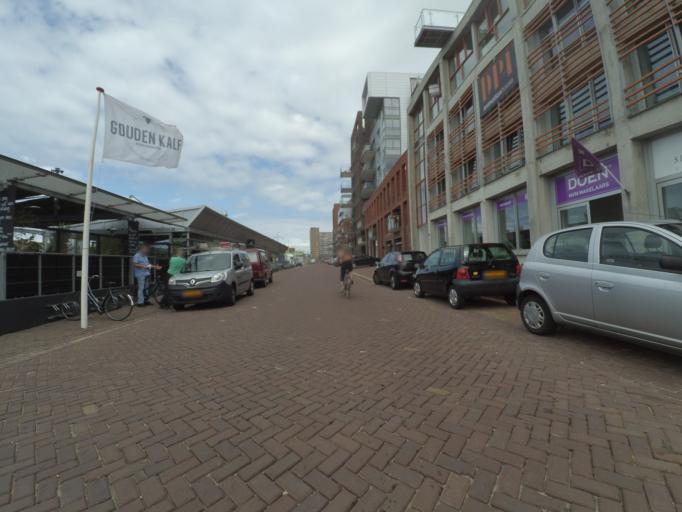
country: NL
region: South Holland
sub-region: Gemeente Den Haag
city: Scheveningen
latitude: 52.0981
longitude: 4.2705
